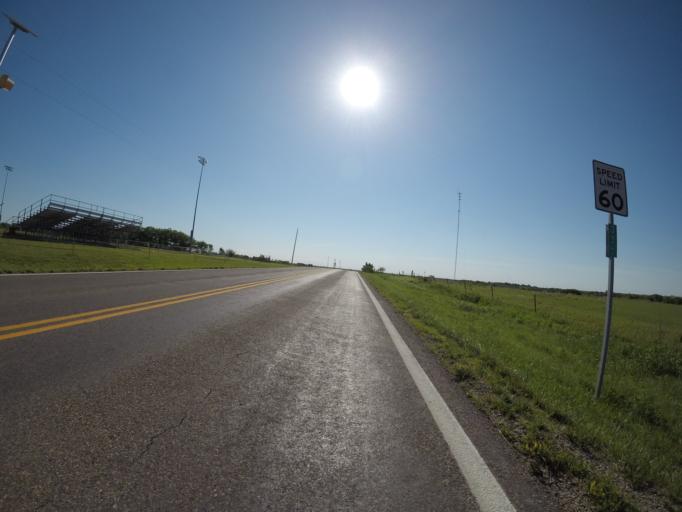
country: US
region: Kansas
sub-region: Lyon County
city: Emporia
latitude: 38.6588
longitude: -96.1483
